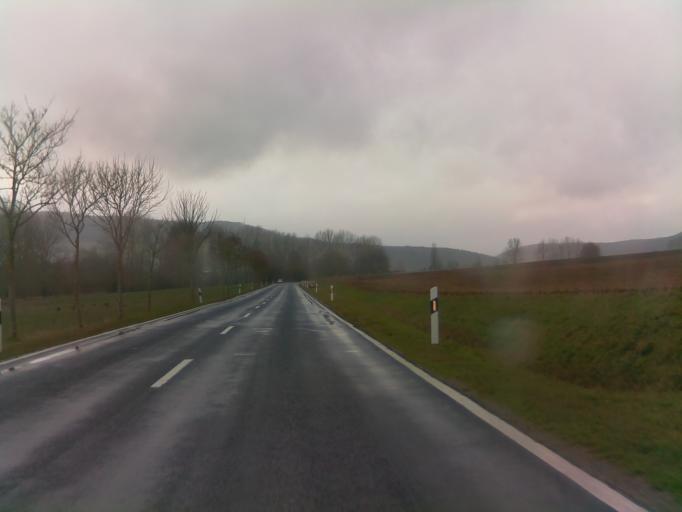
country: DE
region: Thuringia
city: Juchsen
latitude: 50.4724
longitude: 10.5226
